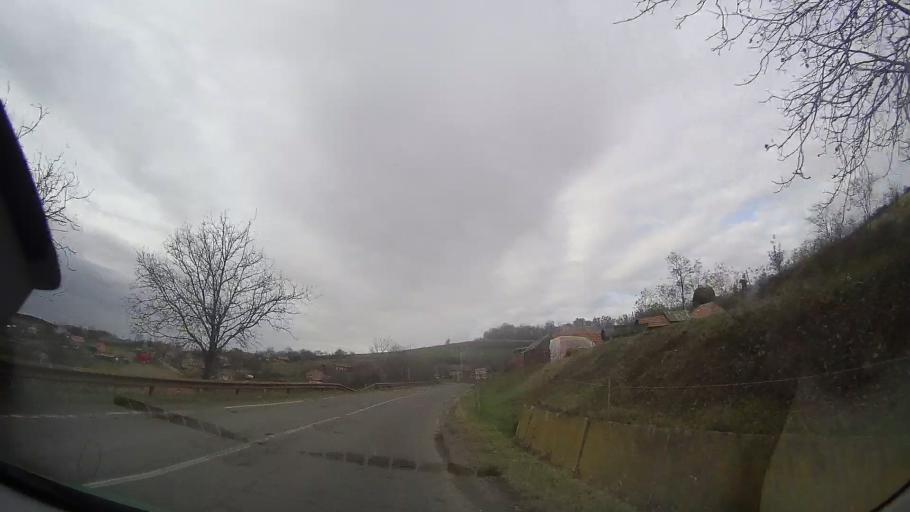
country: RO
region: Bistrita-Nasaud
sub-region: Comuna Silvasu de Campie
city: Silvasu de Campie
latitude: 46.7777
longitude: 24.3195
